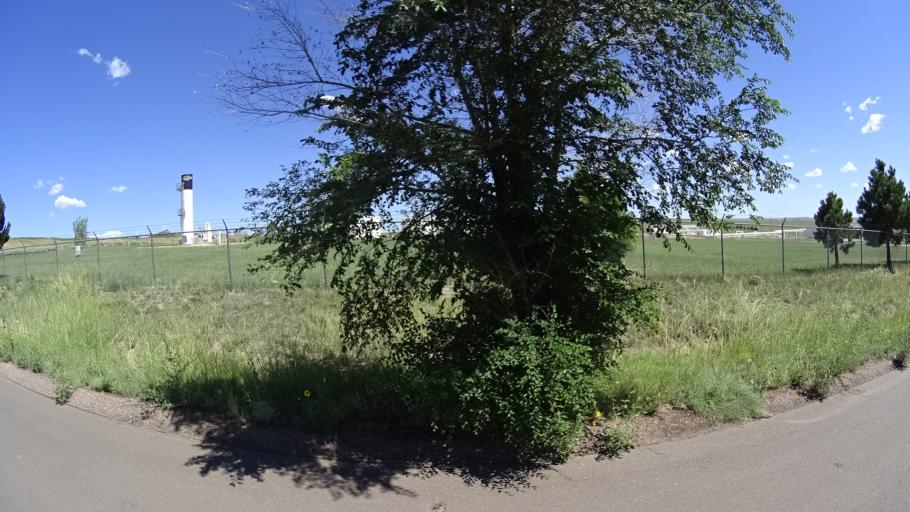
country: US
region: Colorado
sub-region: El Paso County
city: Security-Widefield
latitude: 38.7810
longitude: -104.6776
